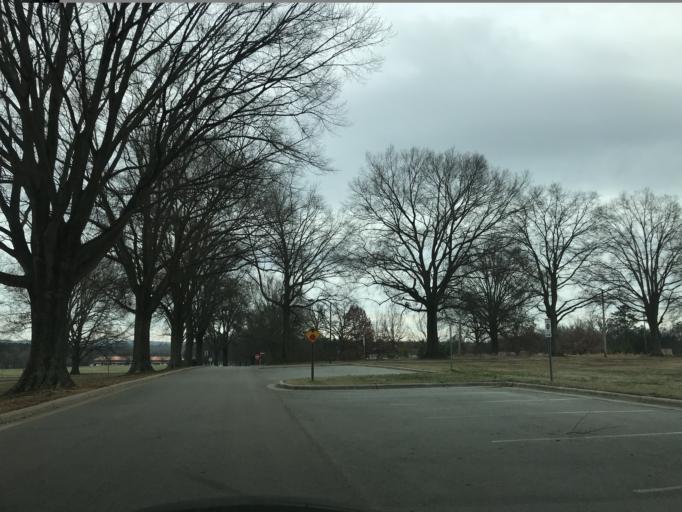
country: US
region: North Carolina
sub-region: Wake County
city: West Raleigh
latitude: 35.7714
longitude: -78.6657
